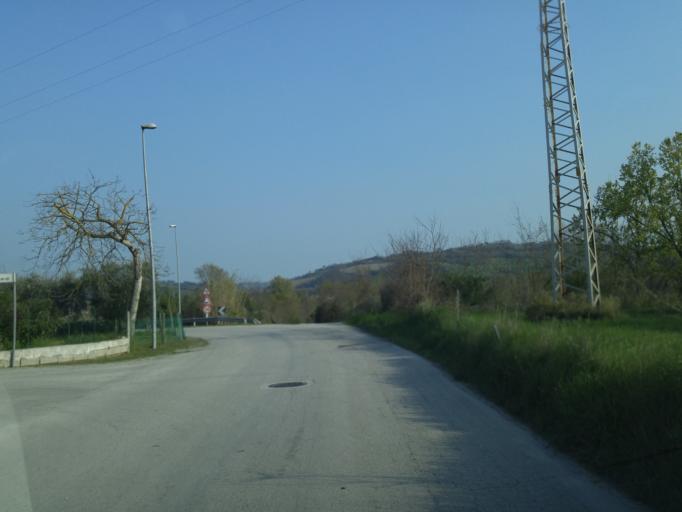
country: IT
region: The Marches
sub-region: Provincia di Pesaro e Urbino
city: Tavernelle
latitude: 43.7342
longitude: 12.8966
